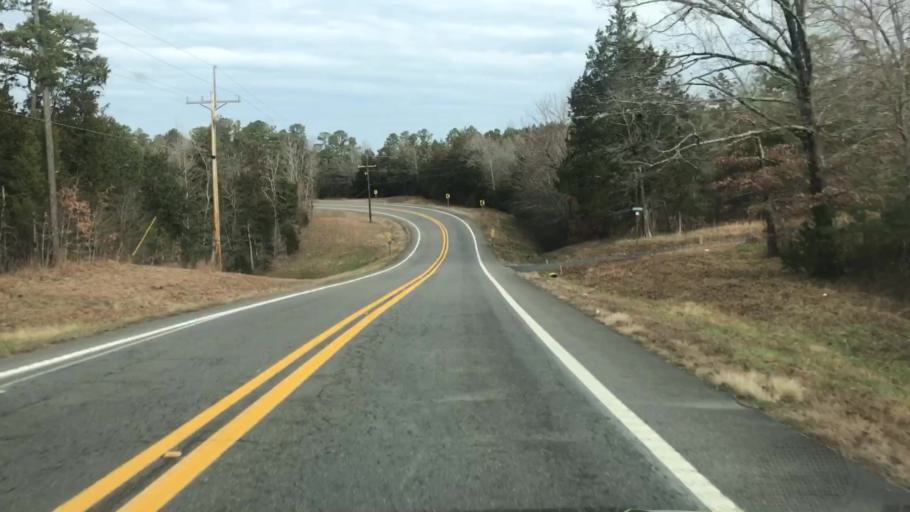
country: US
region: Arkansas
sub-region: Montgomery County
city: Mount Ida
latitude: 34.6177
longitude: -93.7038
